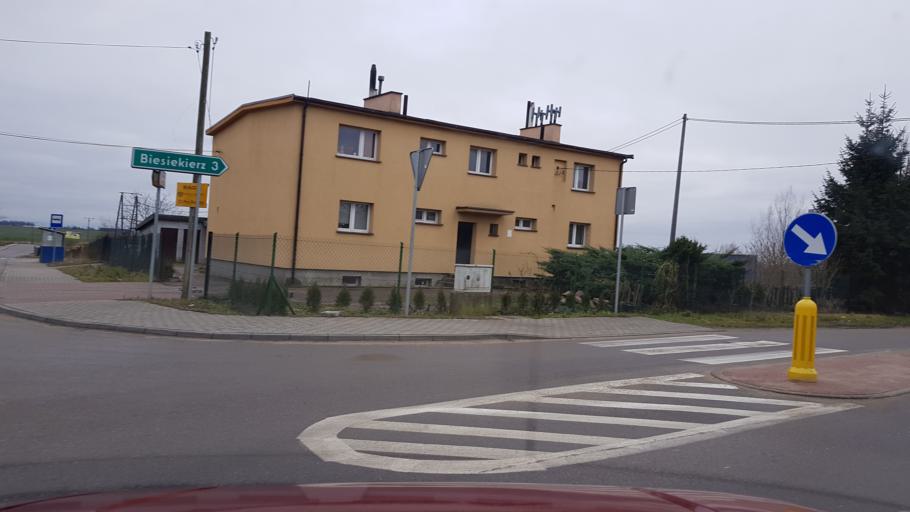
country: PL
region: West Pomeranian Voivodeship
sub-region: Powiat koszalinski
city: Mielno
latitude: 54.1627
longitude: 16.0378
